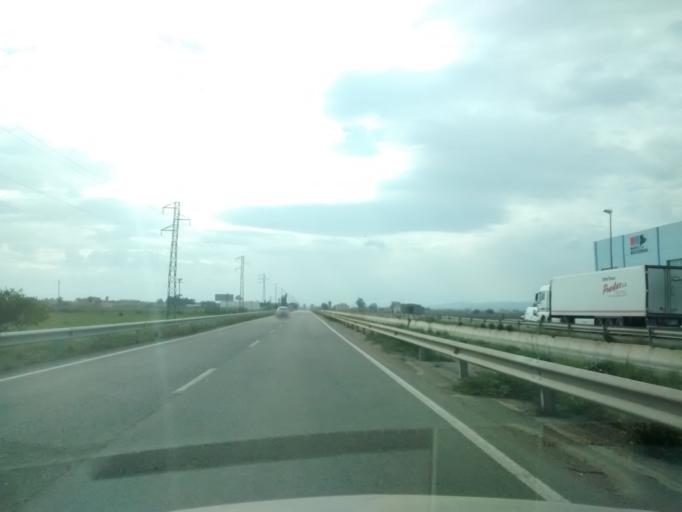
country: ES
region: Catalonia
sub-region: Provincia de Tarragona
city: Deltebre
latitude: 40.7250
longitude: 0.7190
